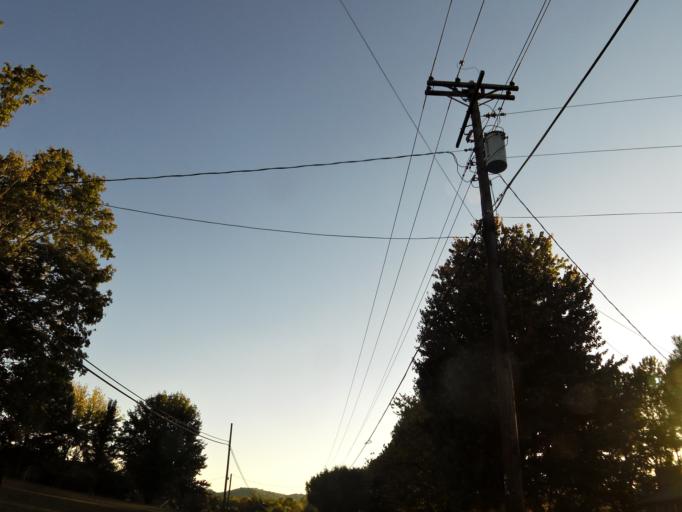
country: US
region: Tennessee
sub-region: Anderson County
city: Clinton
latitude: 36.0104
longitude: -84.0557
